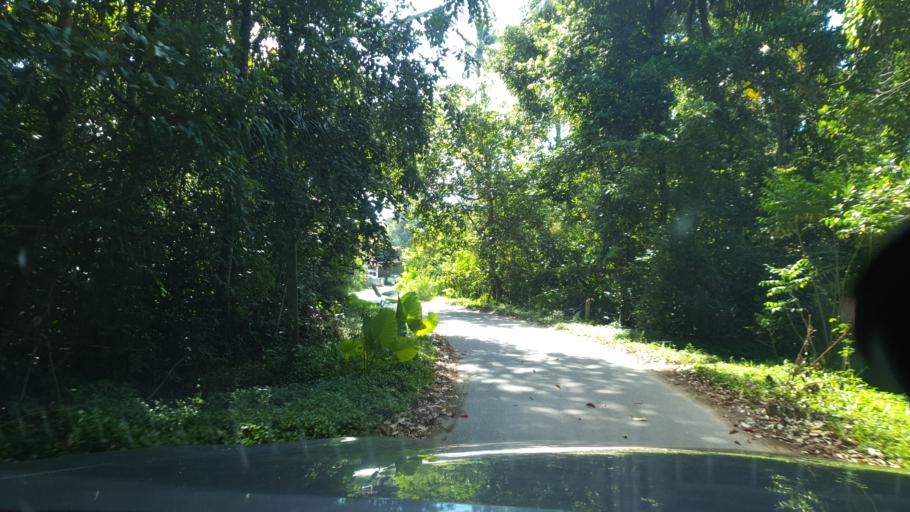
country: TH
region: Krabi
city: Krabi
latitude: 8.0233
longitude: 98.8791
